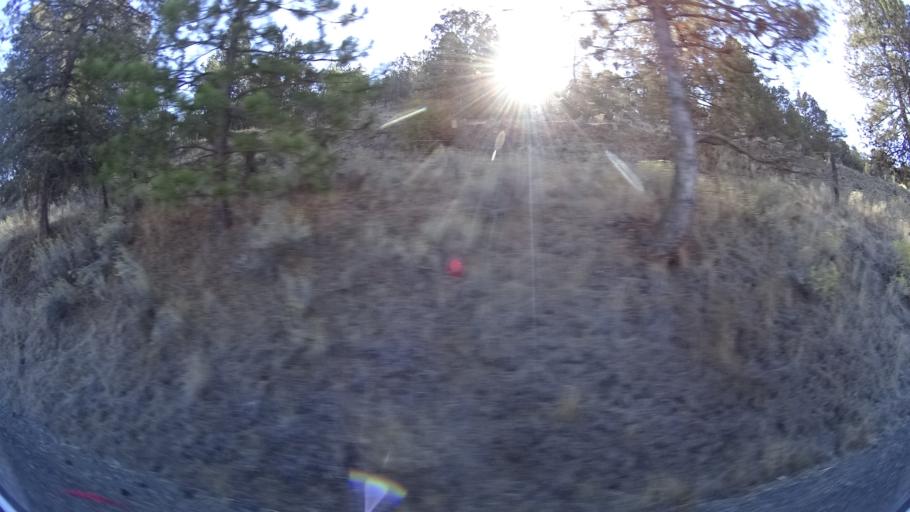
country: US
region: California
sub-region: Siskiyou County
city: Yreka
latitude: 41.5315
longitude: -122.8410
